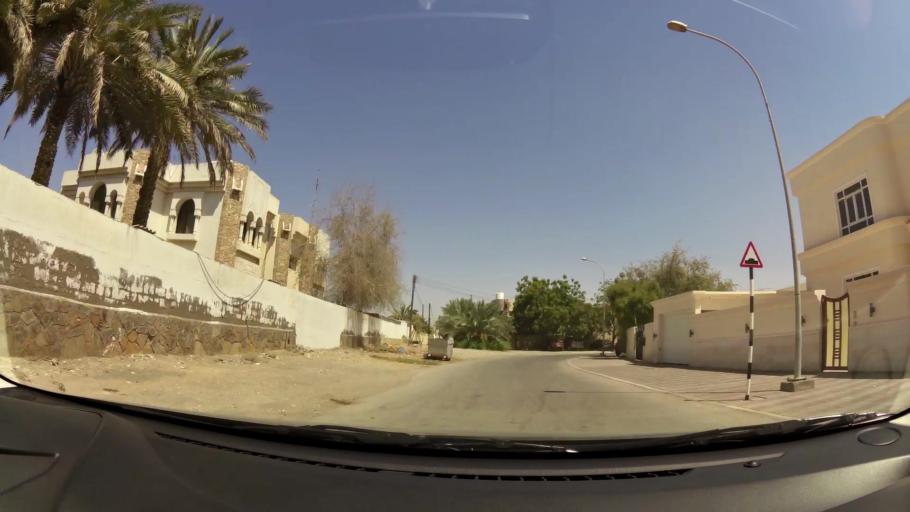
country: OM
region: Muhafazat Masqat
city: As Sib al Jadidah
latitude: 23.6285
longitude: 58.2323
